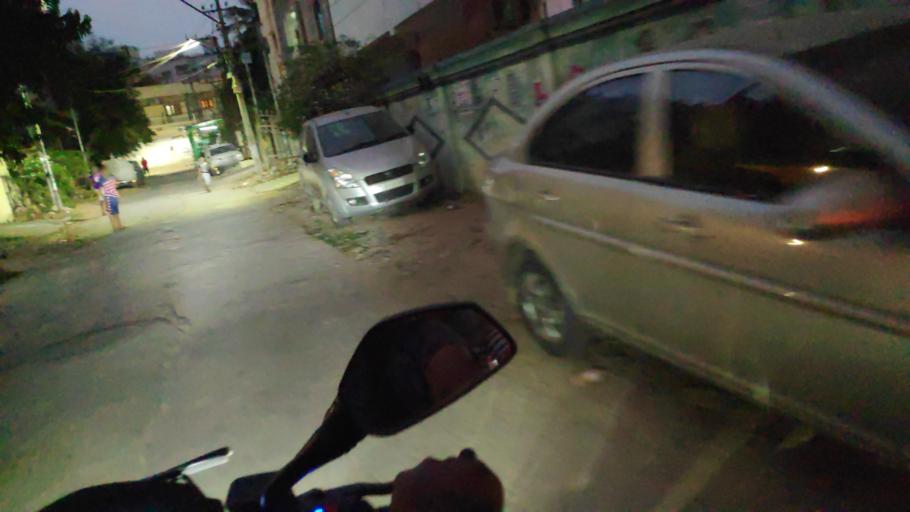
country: IN
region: Telangana
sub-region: Rangareddi
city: Kukatpalli
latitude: 17.4822
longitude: 78.4109
